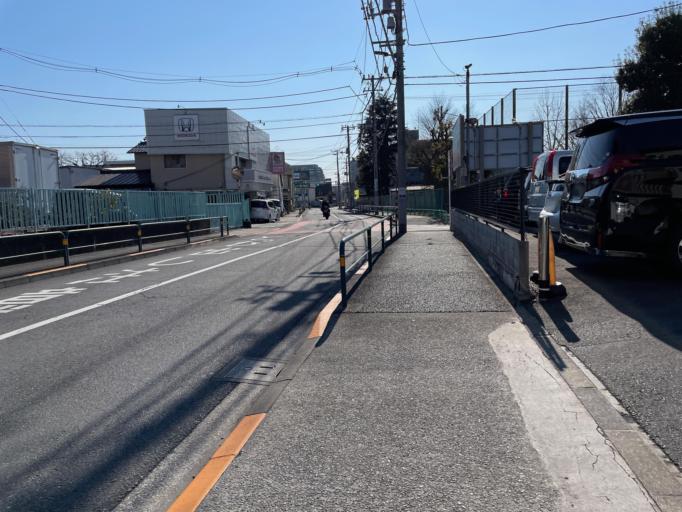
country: JP
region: Saitama
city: Soka
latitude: 35.7858
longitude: 139.7835
